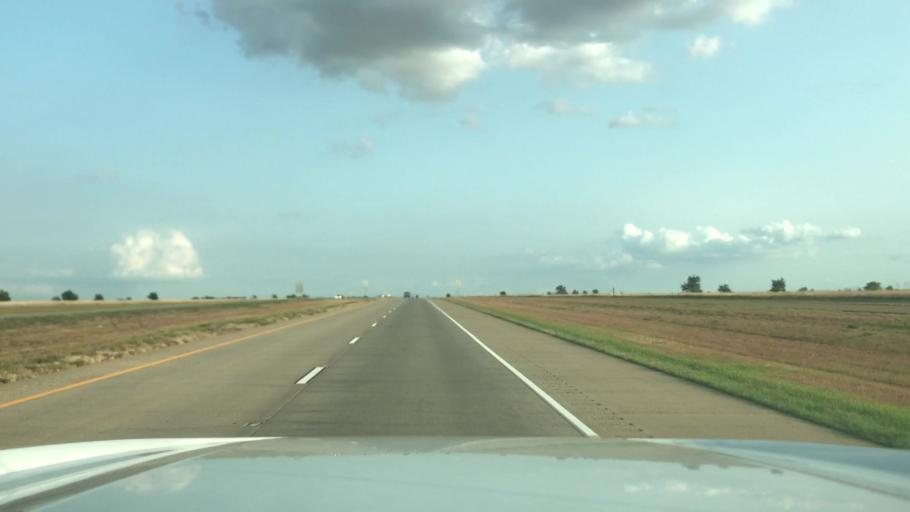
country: US
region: Texas
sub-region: Swisher County
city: Tulia
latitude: 34.5123
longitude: -101.7925
